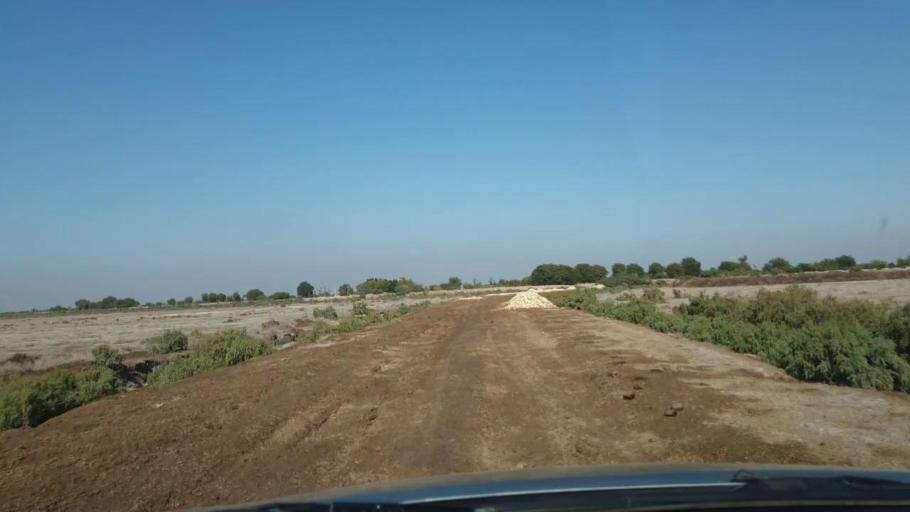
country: PK
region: Sindh
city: Jhol
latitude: 25.9298
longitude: 68.9471
